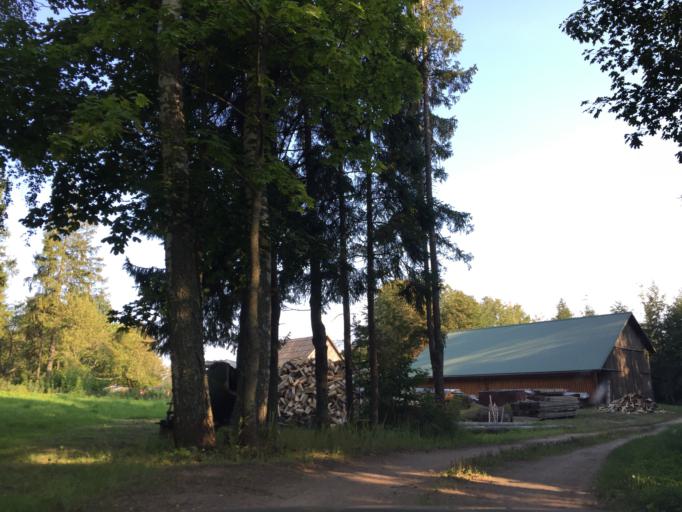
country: LV
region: Limbazu Rajons
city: Limbazi
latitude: 57.5614
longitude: 24.7858
